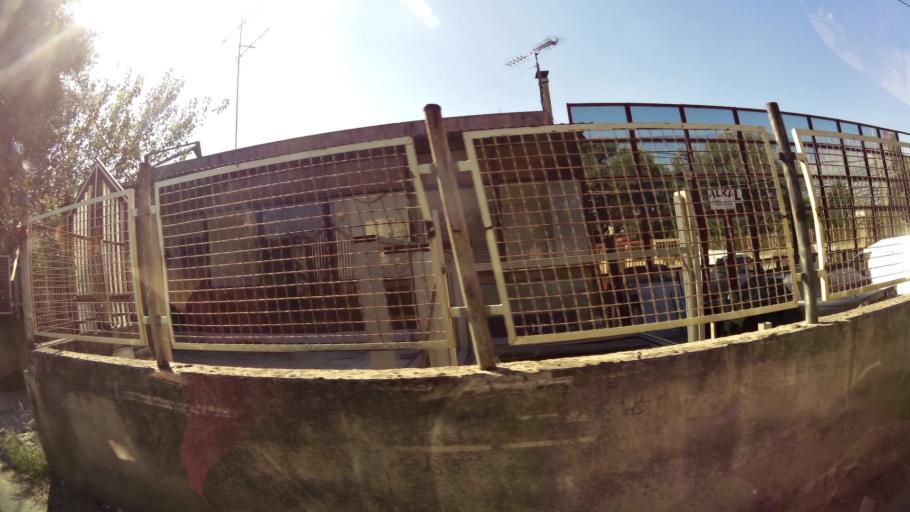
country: GR
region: Attica
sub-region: Nomarchia Athinas
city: Lykovrysi
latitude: 38.0732
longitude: 23.7805
